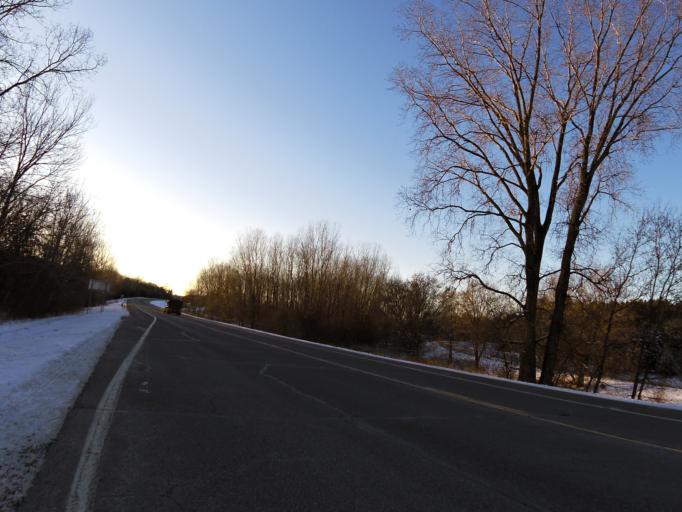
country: US
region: Minnesota
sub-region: Washington County
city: Lake Elmo
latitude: 44.9645
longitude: -92.8441
